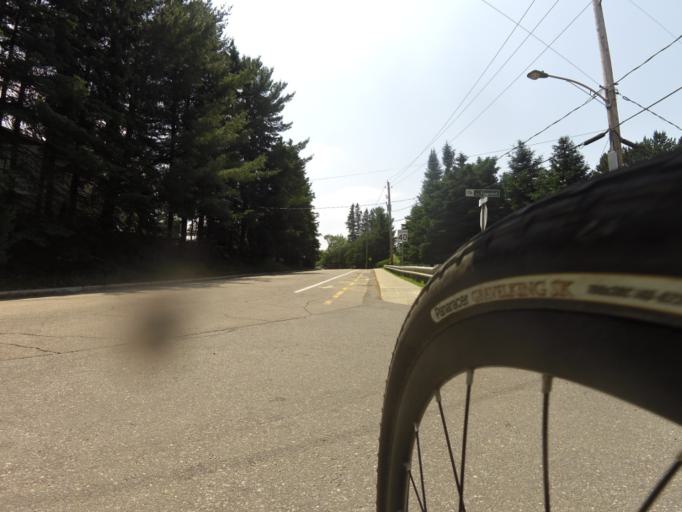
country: CA
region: Quebec
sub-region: Laurentides
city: Mont-Tremblant
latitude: 46.1252
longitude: -74.5916
